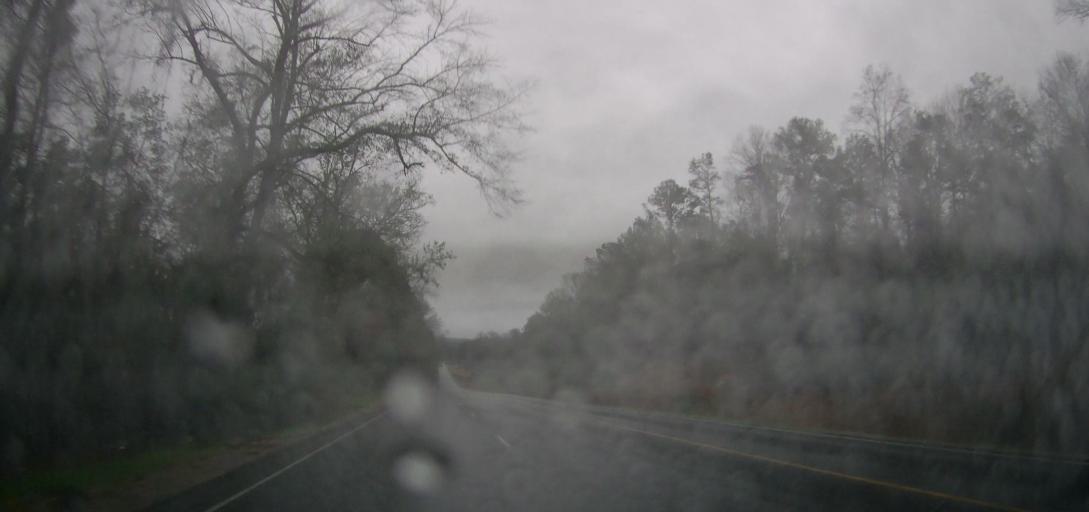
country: US
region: Alabama
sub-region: Autauga County
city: Pine Level
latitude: 32.5779
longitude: -86.6870
